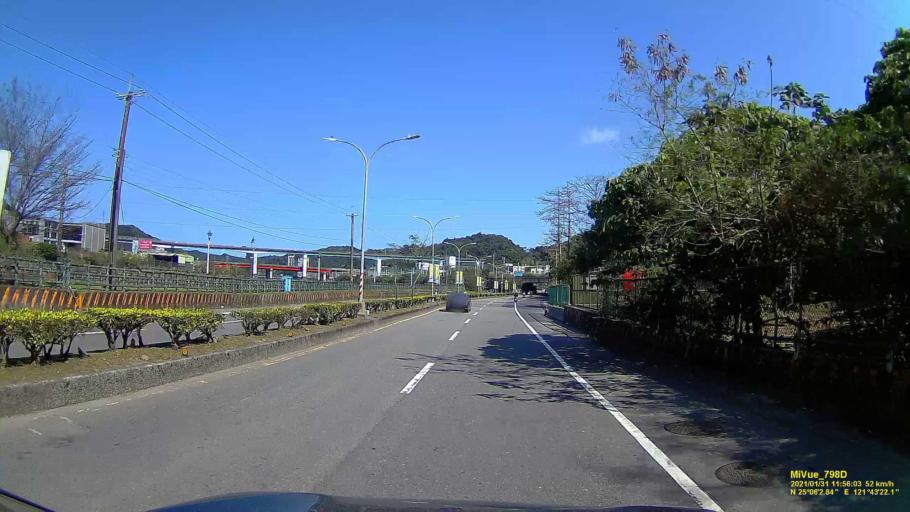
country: TW
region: Taiwan
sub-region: Keelung
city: Keelung
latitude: 25.1009
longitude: 121.7229
